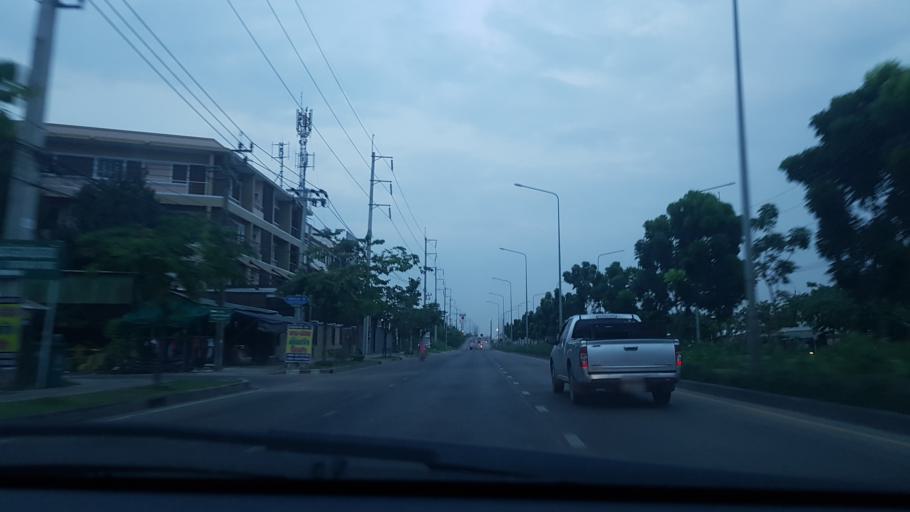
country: TH
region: Bangkok
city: Nong Khaem
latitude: 13.7232
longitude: 100.3638
